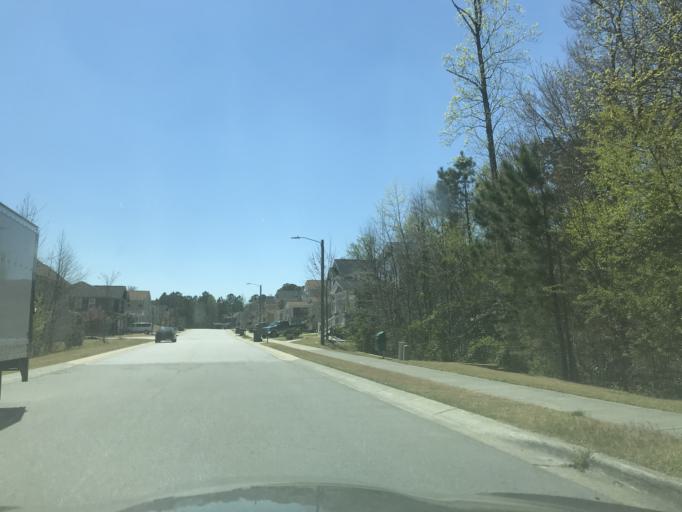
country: US
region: North Carolina
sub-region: Wake County
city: Knightdale
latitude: 35.8533
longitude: -78.5617
